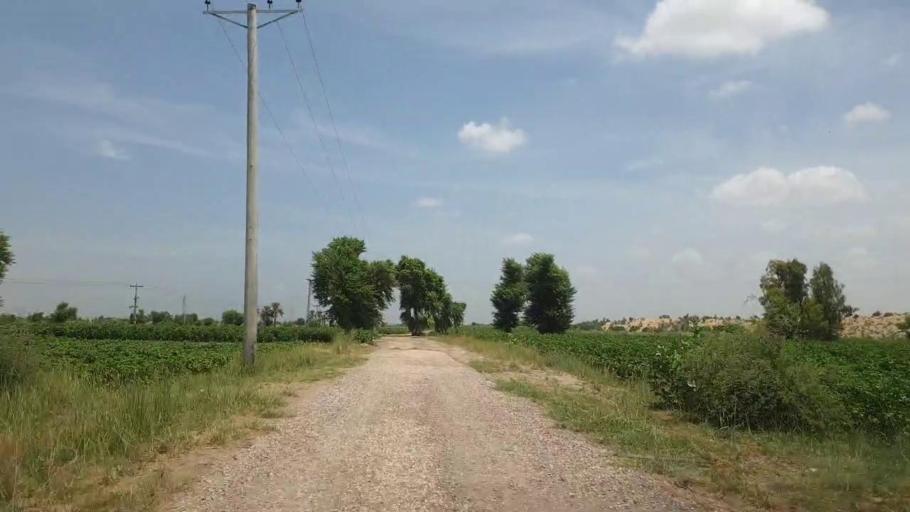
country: PK
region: Sindh
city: Kot Diji
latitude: 27.1513
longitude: 69.0173
